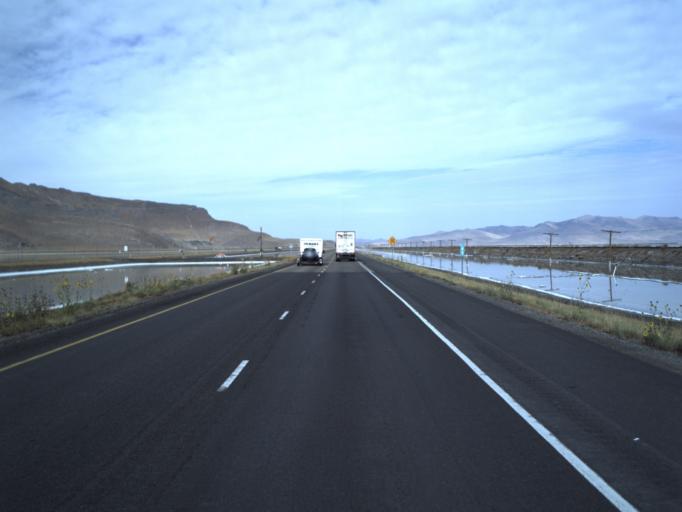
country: US
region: Utah
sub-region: Tooele County
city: Grantsville
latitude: 40.7299
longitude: -112.5867
